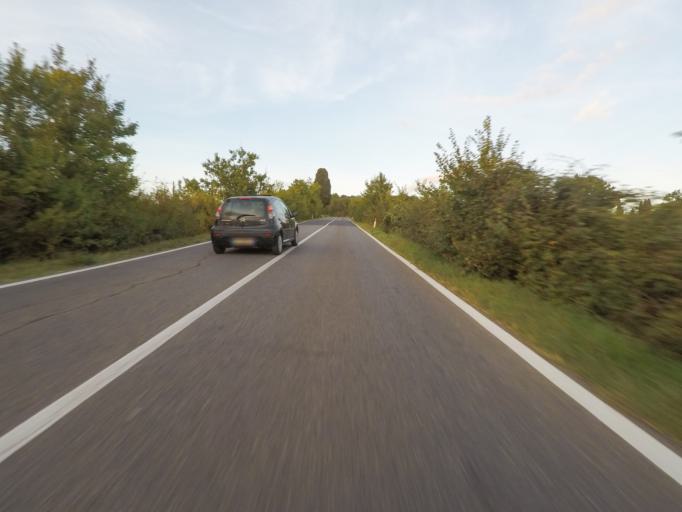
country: IT
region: Tuscany
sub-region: Provincia di Siena
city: Pienza
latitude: 43.0986
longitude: 11.6952
